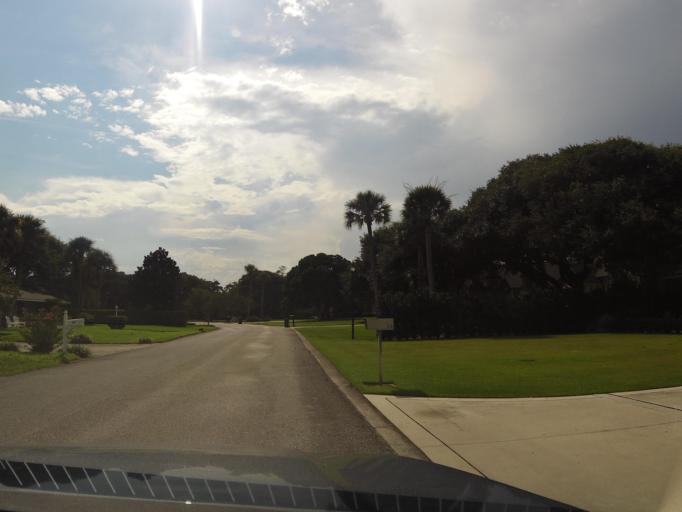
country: US
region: Florida
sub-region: Saint Johns County
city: Ponte Vedra Beach
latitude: 30.2487
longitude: -81.3837
